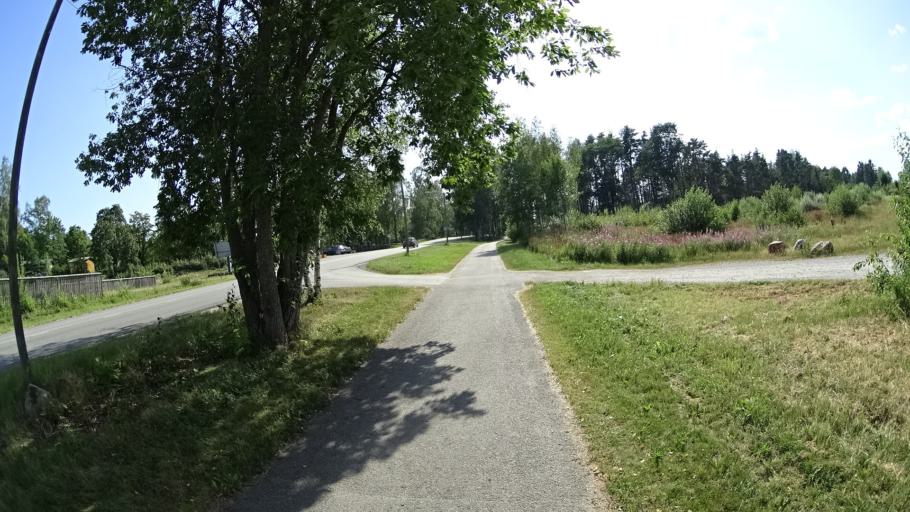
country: FI
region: Uusimaa
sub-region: Porvoo
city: Porvoo
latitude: 60.3938
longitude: 25.6447
